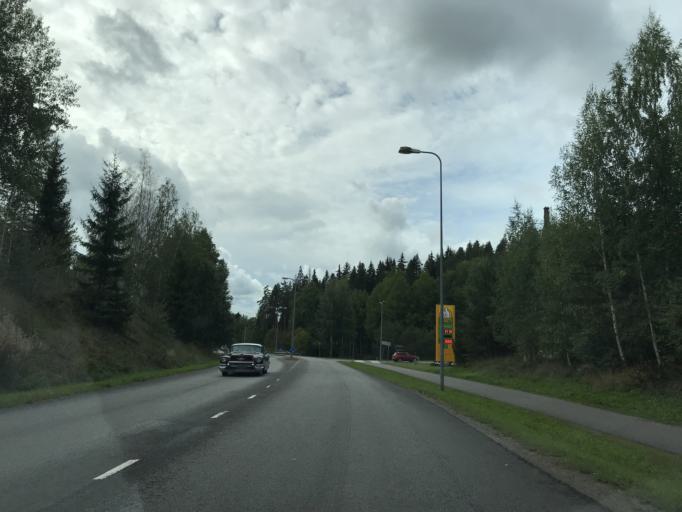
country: FI
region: Paijanne Tavastia
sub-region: Lahti
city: Lahti
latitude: 61.0013
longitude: 25.7572
